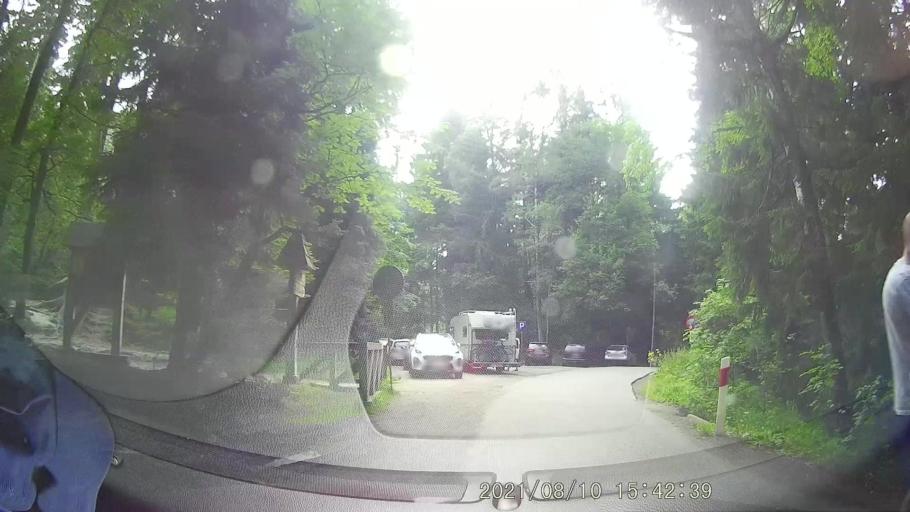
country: CZ
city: Machov
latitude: 50.4869
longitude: 16.3362
